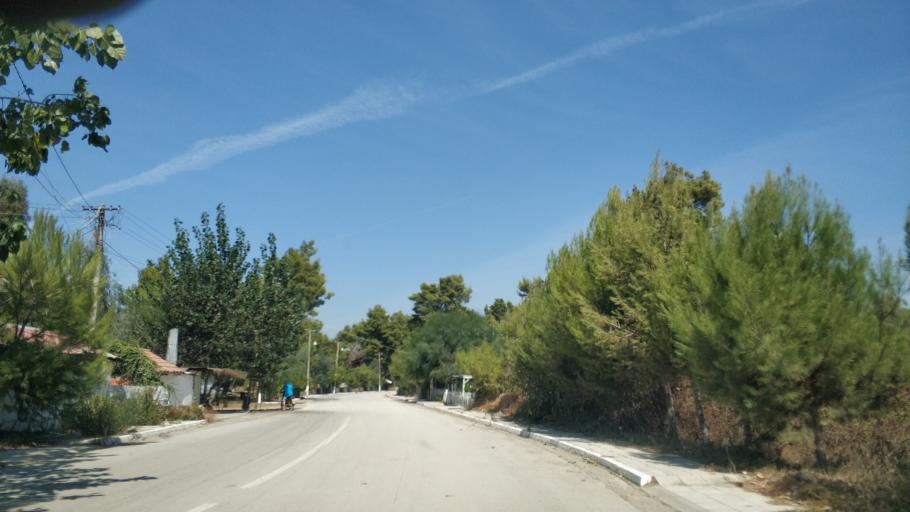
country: AL
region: Fier
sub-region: Rrethi i Lushnjes
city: Divjake
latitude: 40.9672
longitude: 19.4785
